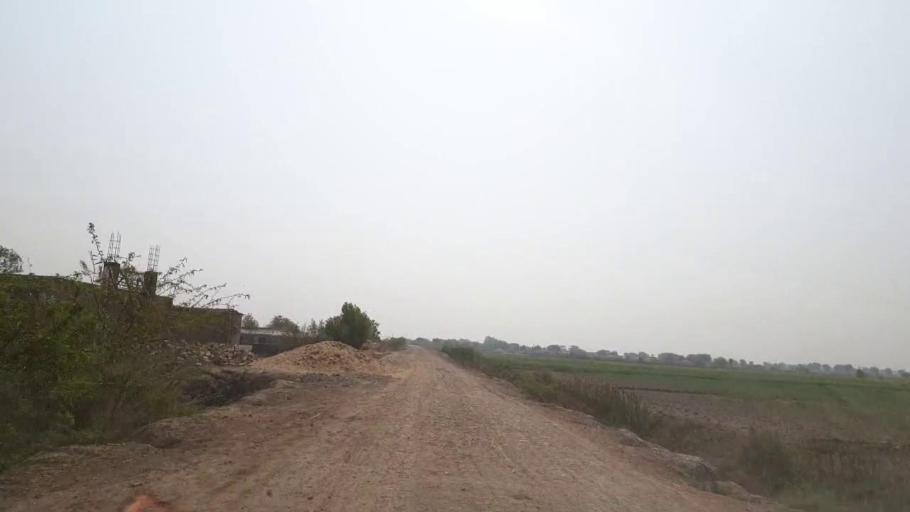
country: PK
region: Sindh
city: Mirpur Khas
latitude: 25.5392
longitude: 69.0621
